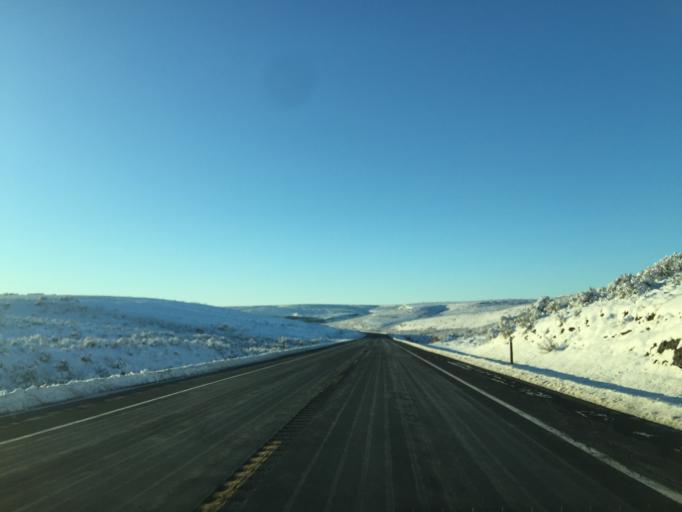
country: US
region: Washington
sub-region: Grant County
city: Soap Lake
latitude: 47.6052
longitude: -119.6361
